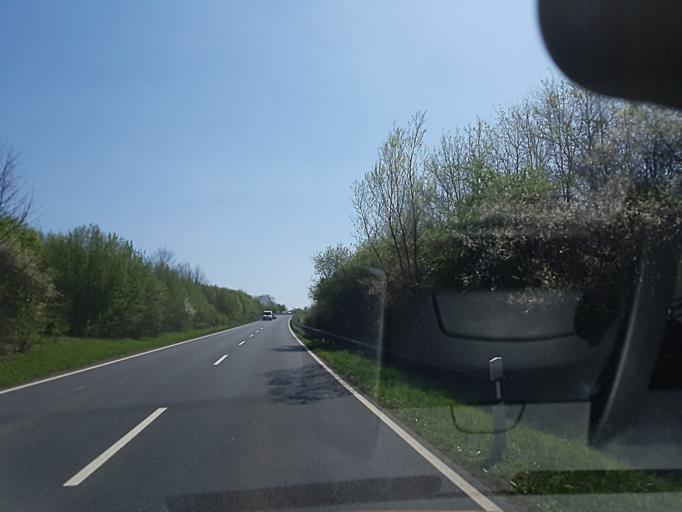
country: DE
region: Saxony
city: Leisnig
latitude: 51.1640
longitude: 12.9093
